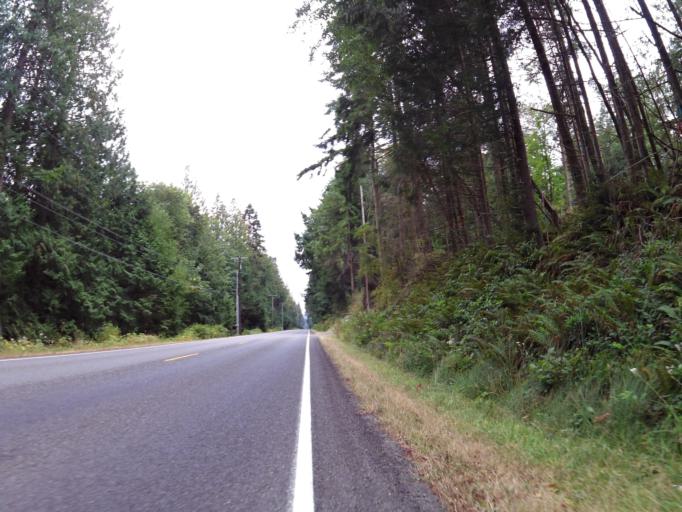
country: US
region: Washington
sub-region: Jefferson County
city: Port Hadlock-Irondale
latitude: 48.0016
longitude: -122.7243
